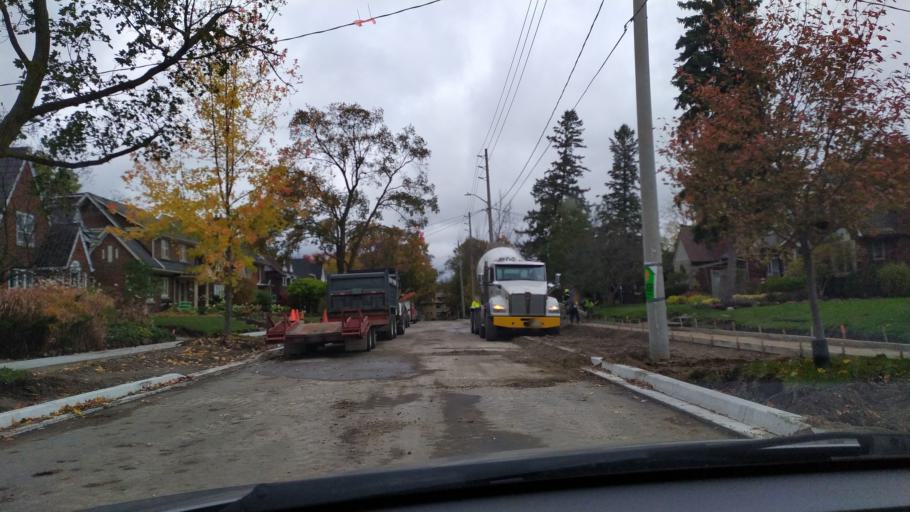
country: CA
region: Ontario
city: Waterloo
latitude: 43.4531
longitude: -80.5197
